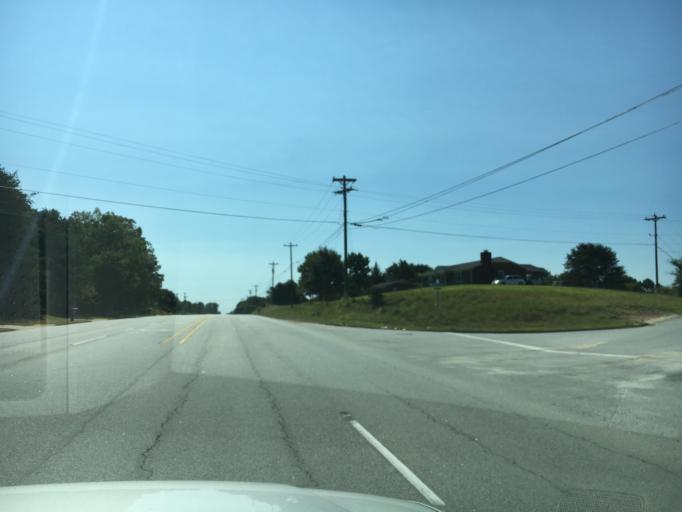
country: US
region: South Carolina
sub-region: Spartanburg County
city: Roebuck
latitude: 34.8443
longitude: -82.0044
